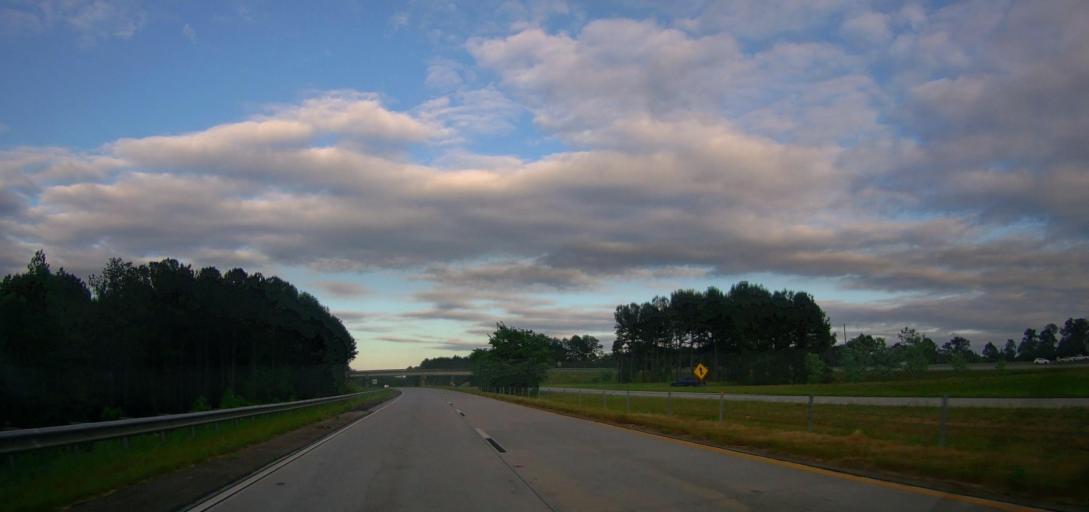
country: US
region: Georgia
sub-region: Oconee County
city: Watkinsville
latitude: 33.9137
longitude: -83.4542
